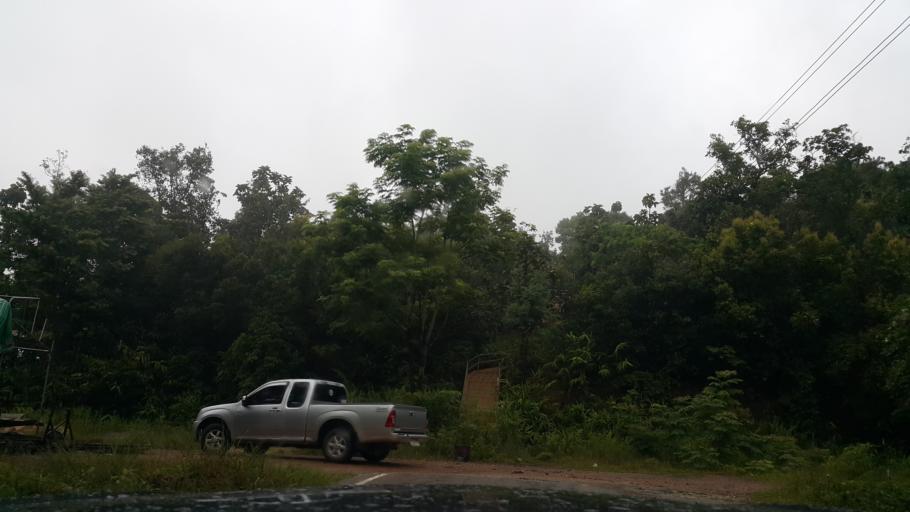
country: TH
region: Phayao
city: Phu Sang
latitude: 19.6051
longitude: 100.4123
